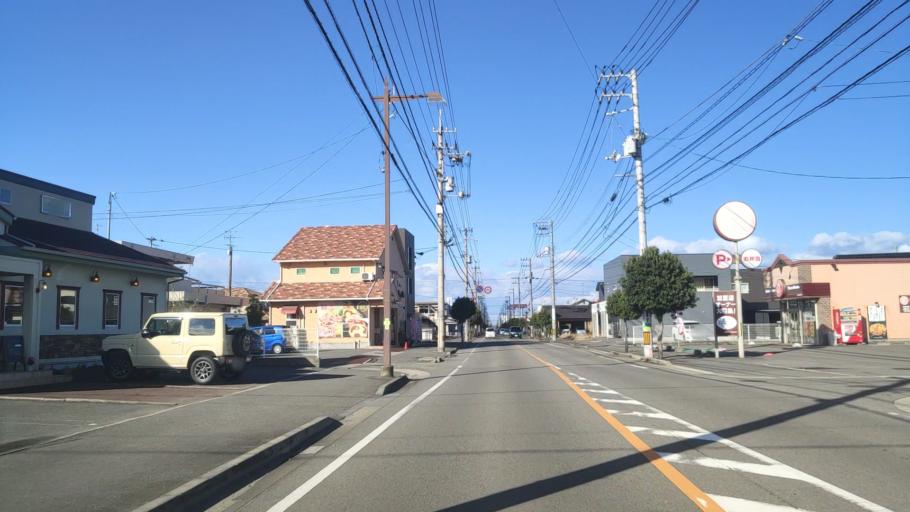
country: JP
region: Ehime
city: Saijo
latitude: 33.9221
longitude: 133.1916
